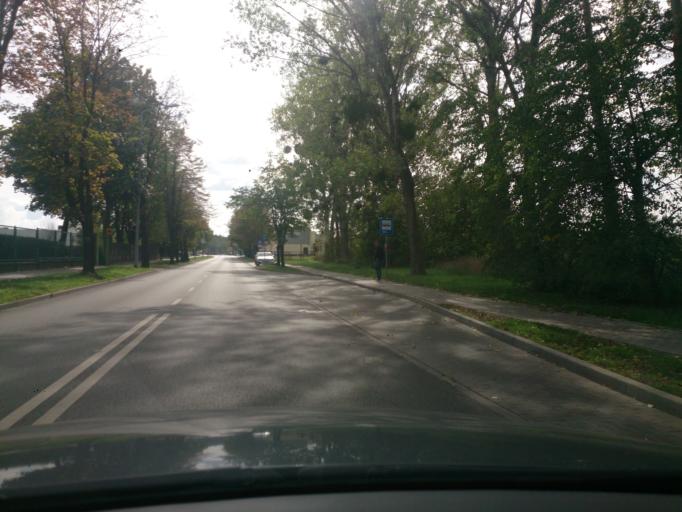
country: PL
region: Kujawsko-Pomorskie
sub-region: Grudziadz
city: Grudziadz
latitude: 53.4714
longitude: 18.7520
